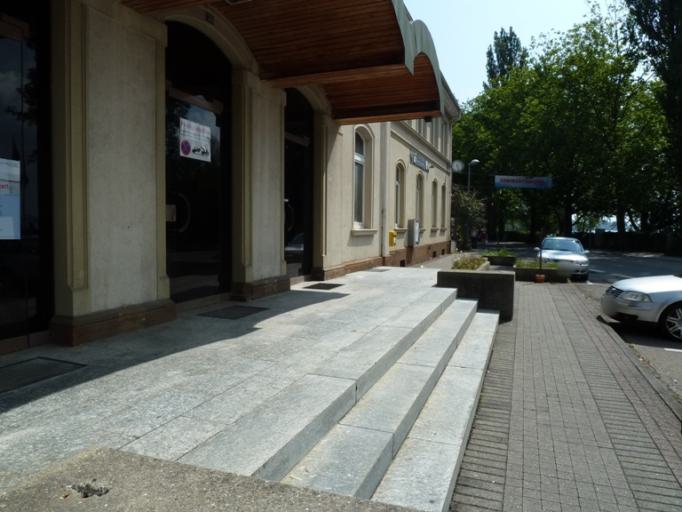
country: DE
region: Baden-Wuerttemberg
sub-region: Tuebingen Region
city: Uberlingen
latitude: 47.7690
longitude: 9.1455
